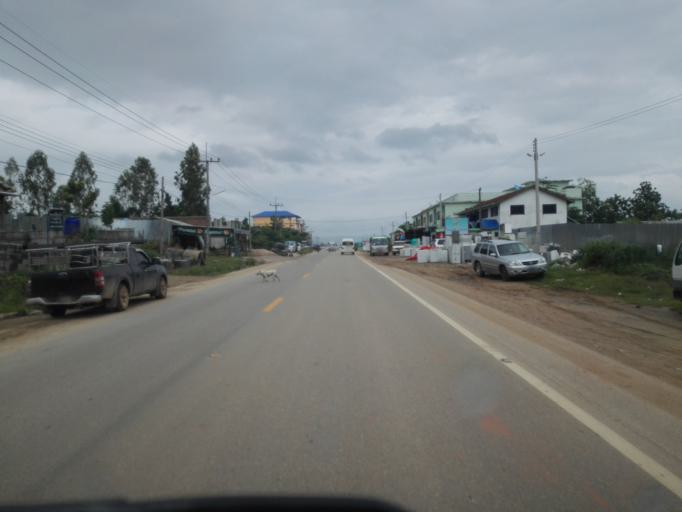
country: TH
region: Tak
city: Mae Sot
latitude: 16.6858
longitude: 98.4879
